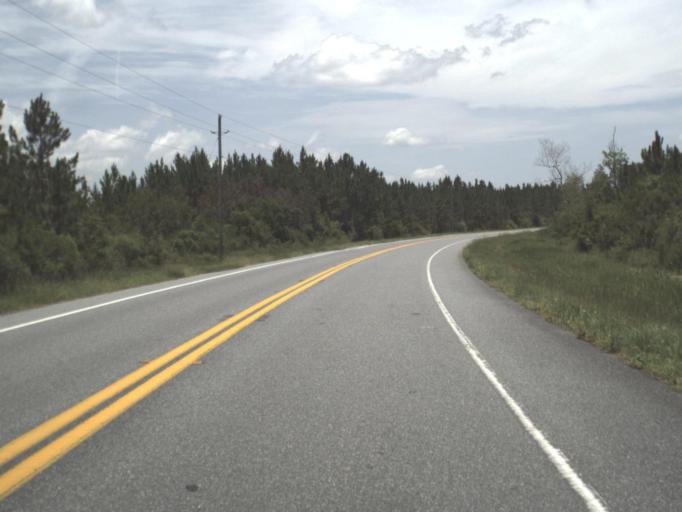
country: US
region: Florida
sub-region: Lafayette County
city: Mayo
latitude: 30.0172
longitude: -83.1943
